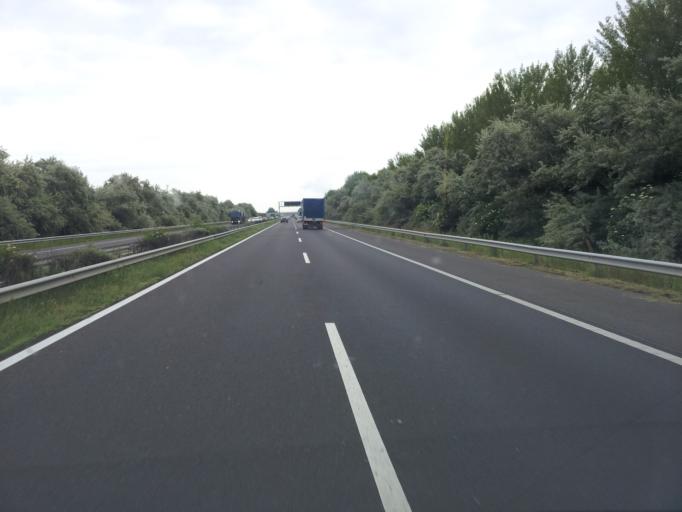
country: HU
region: Heves
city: Fuzesabony
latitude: 47.7300
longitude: 20.3889
